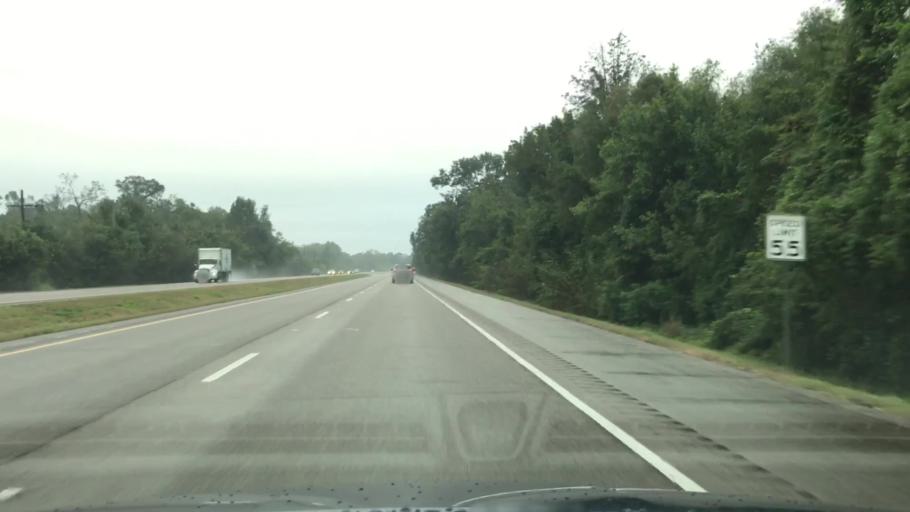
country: US
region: Louisiana
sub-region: Saint Charles Parish
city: Paradis
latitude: 29.8504
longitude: -90.4480
